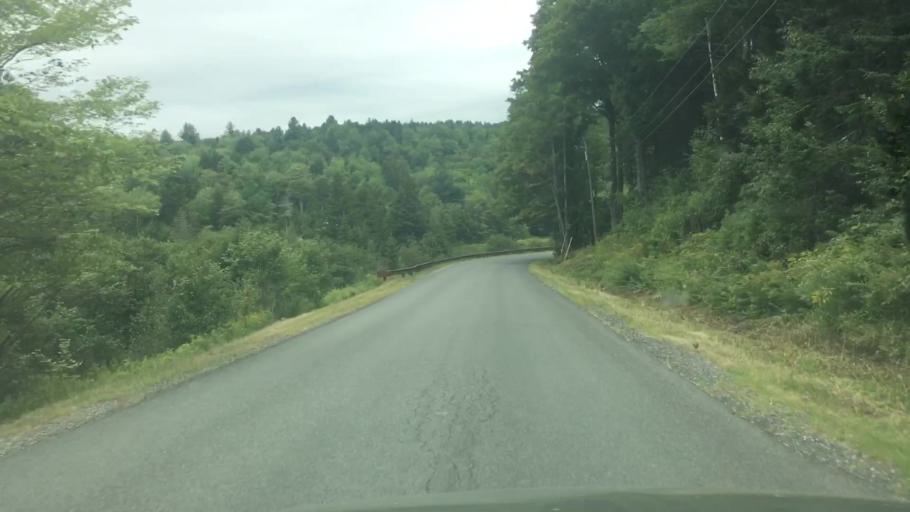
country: US
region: Vermont
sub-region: Windham County
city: Dover
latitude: 42.8487
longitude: -72.8364
